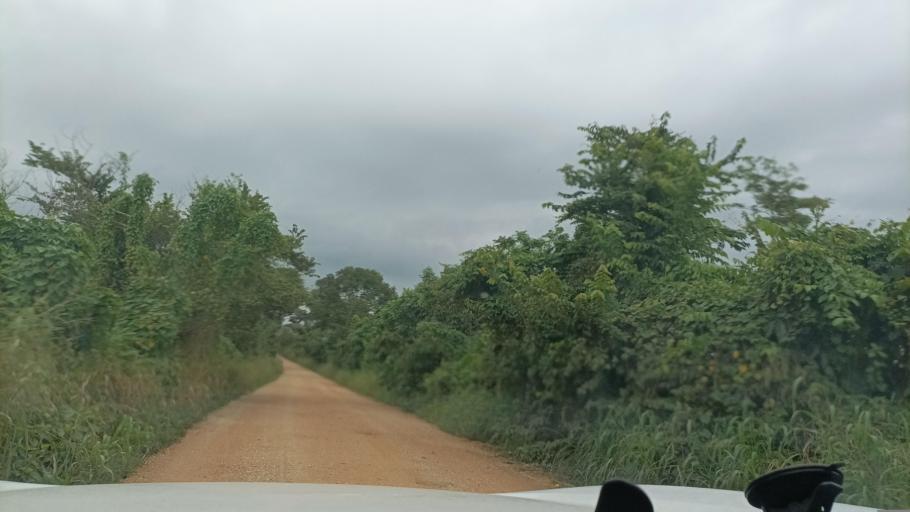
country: MX
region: Veracruz
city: Hidalgotitlan
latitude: 17.6462
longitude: -94.5049
